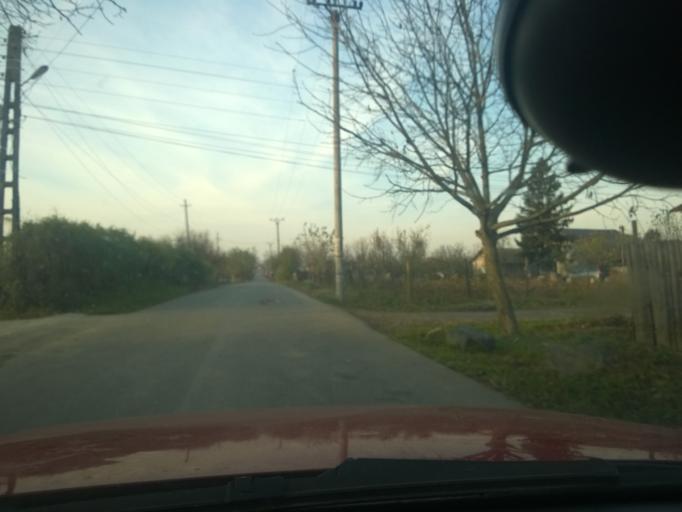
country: RO
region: Giurgiu
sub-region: Comuna Herasti
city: Herasti
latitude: 44.2152
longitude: 26.3589
